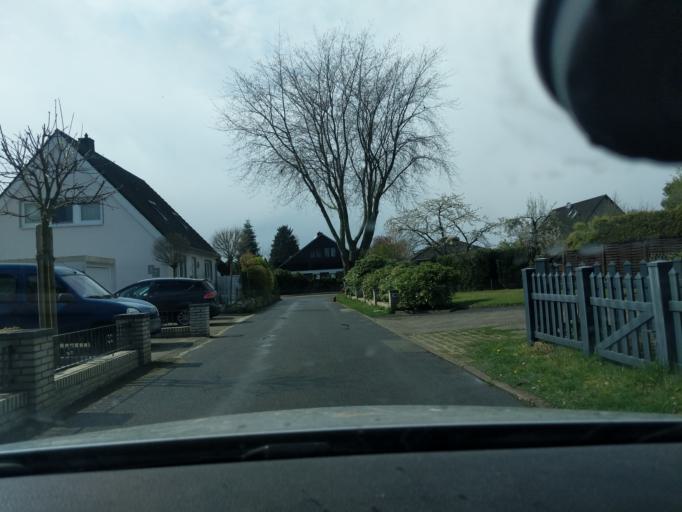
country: DE
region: Lower Saxony
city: Ahlerstedt
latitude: 53.4087
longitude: 9.4519
